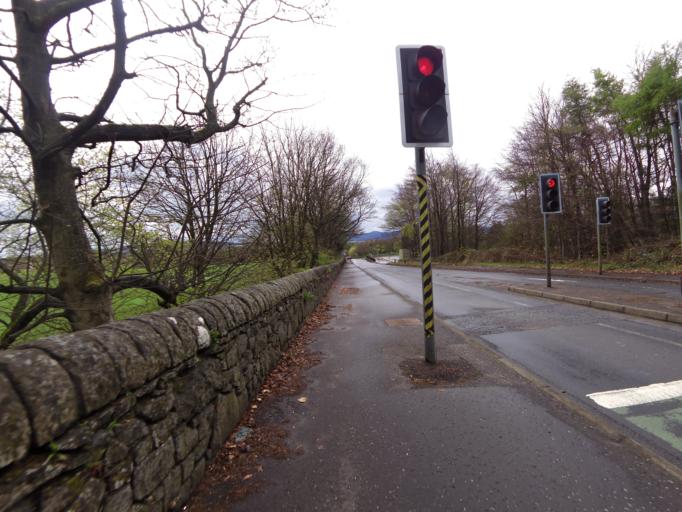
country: GB
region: Scotland
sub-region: Edinburgh
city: Currie
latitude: 55.9688
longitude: -3.3223
